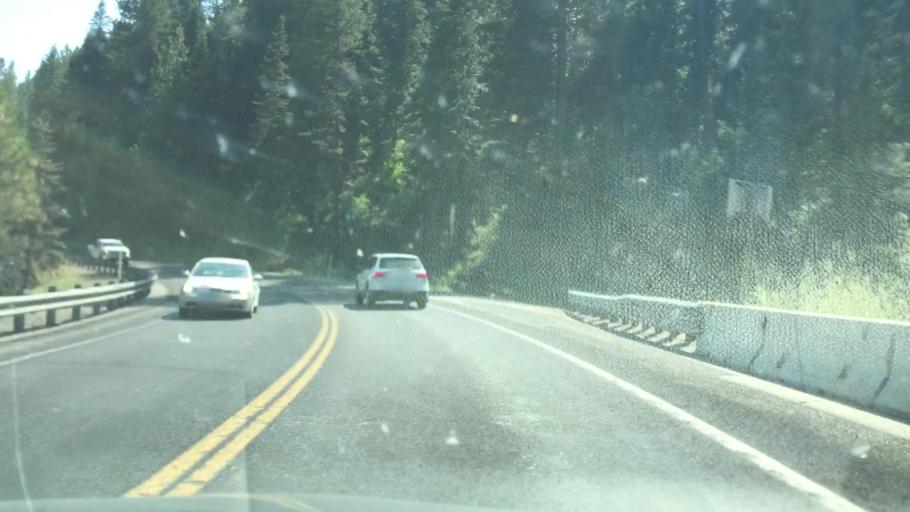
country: US
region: Idaho
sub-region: Valley County
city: Cascade
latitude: 44.2443
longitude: -116.1030
